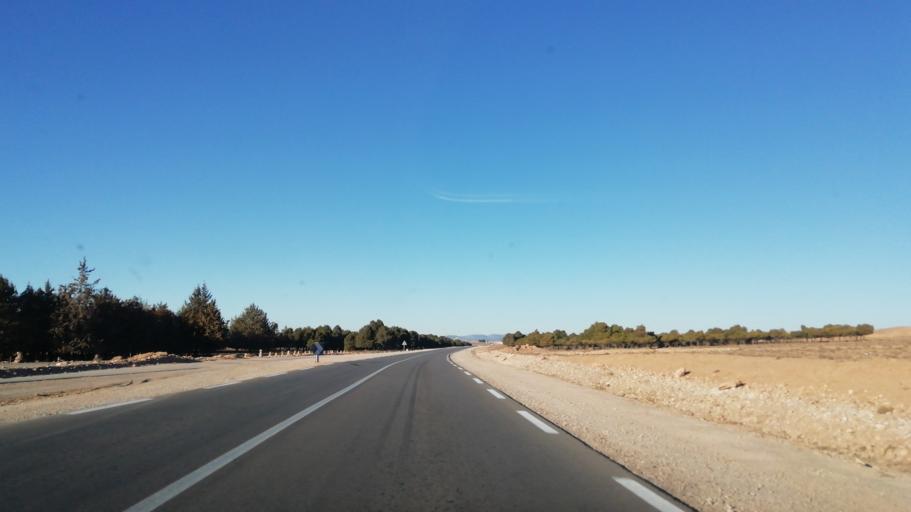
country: DZ
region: Tlemcen
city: Sebdou
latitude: 34.4592
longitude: -1.2755
